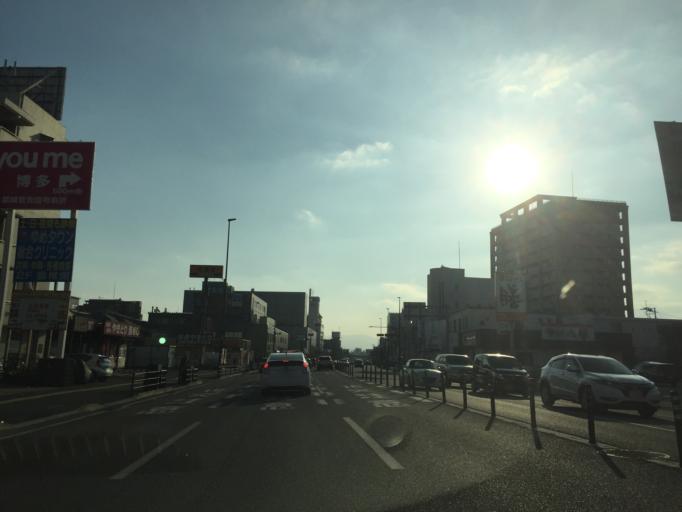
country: JP
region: Fukuoka
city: Fukuoka-shi
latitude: 33.6211
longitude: 130.4191
